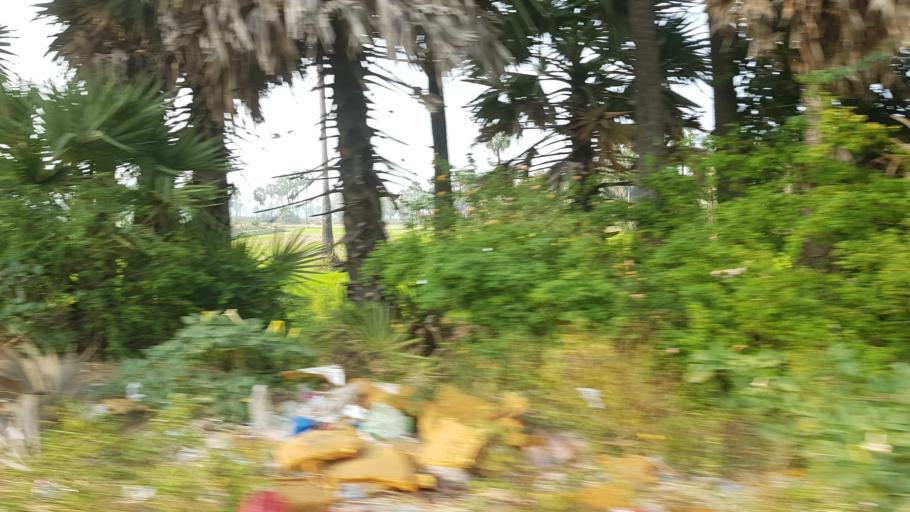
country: IN
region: Andhra Pradesh
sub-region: Krishna
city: Korukollu
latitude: 16.4912
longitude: 81.2556
